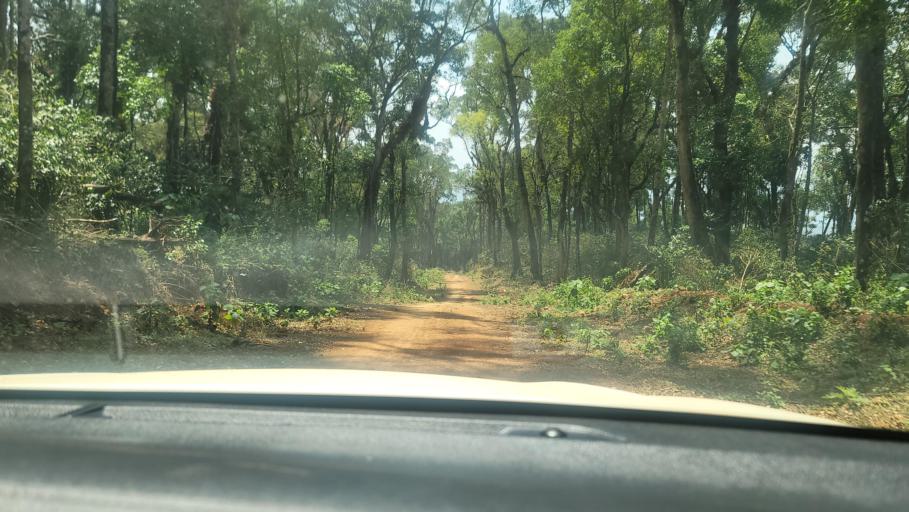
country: ET
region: Southern Nations, Nationalities, and People's Region
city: Bonga
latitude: 7.5416
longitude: 36.1806
